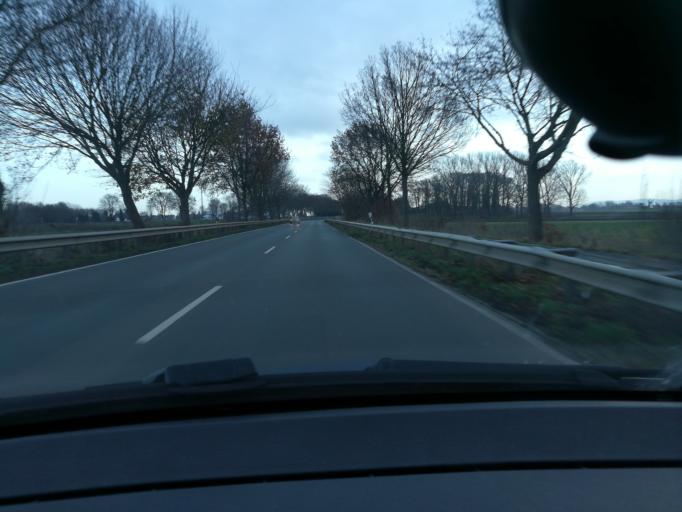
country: DE
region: North Rhine-Westphalia
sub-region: Regierungsbezirk Detmold
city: Hille
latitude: 52.3297
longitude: 8.7665
